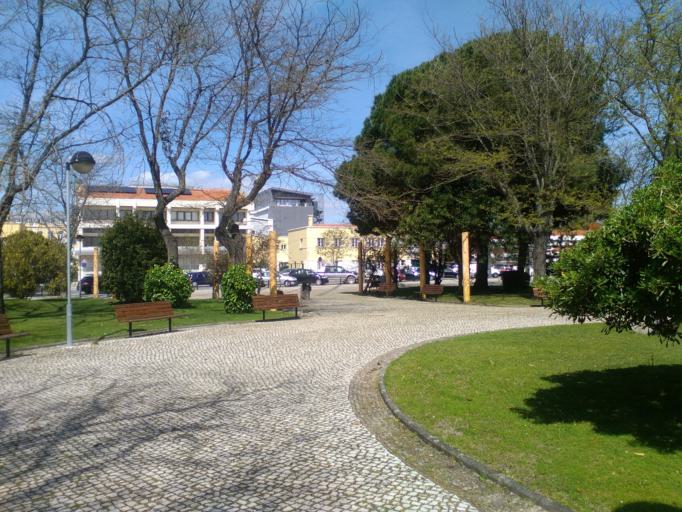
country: PT
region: Setubal
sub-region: Setubal
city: Setubal
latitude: 38.5209
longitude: -8.8910
